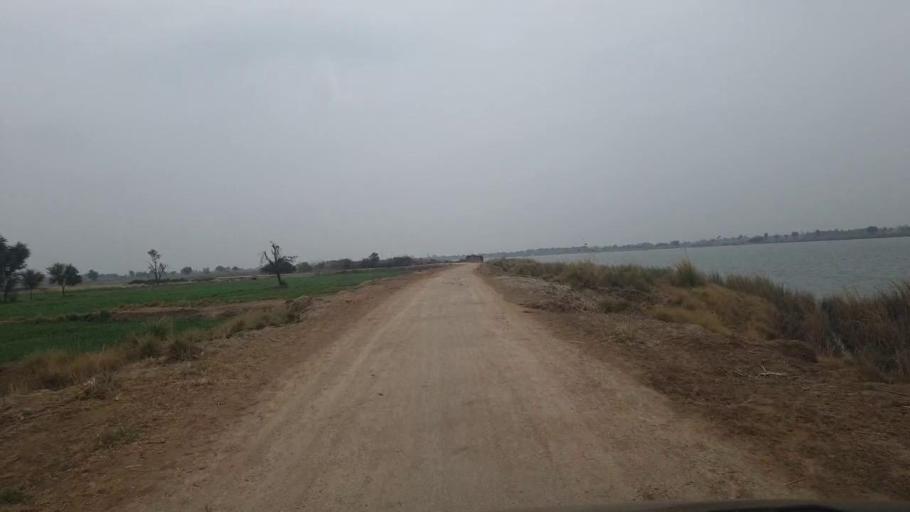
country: PK
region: Sindh
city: Tando Adam
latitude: 25.8464
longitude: 68.6984
